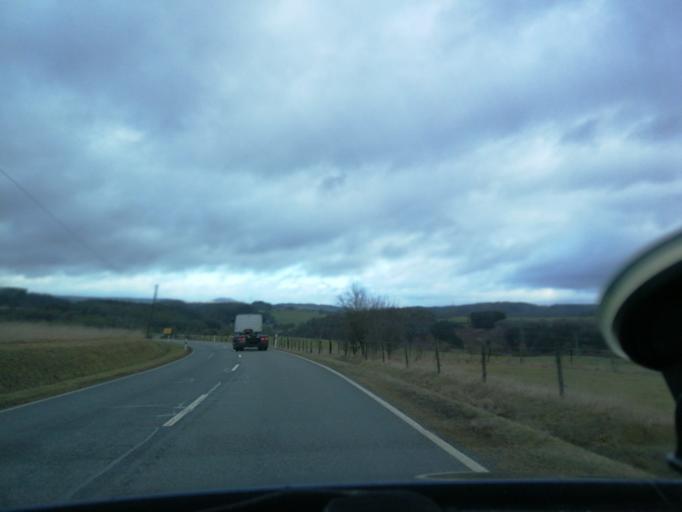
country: DE
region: Rheinland-Pfalz
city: Oberehe-Stroheich
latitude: 50.3091
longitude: 6.7720
